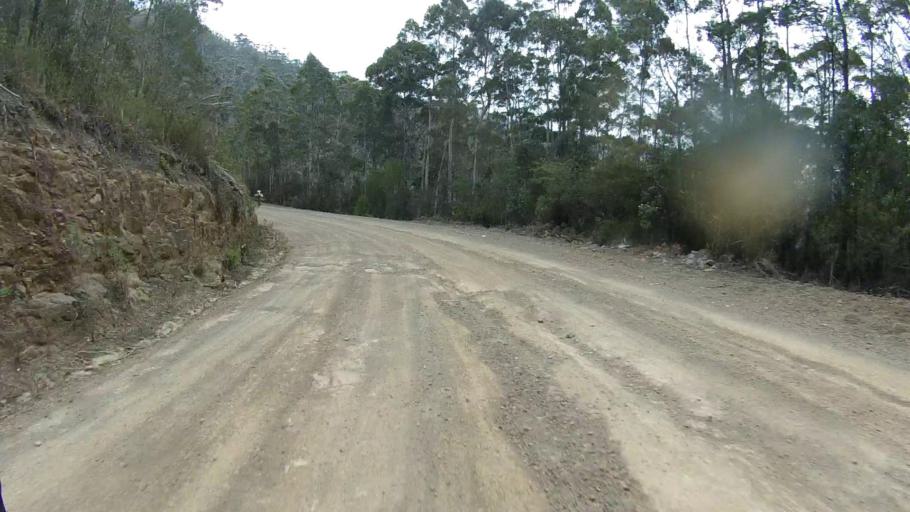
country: AU
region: Tasmania
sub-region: Sorell
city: Sorell
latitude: -42.6976
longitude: 147.8570
